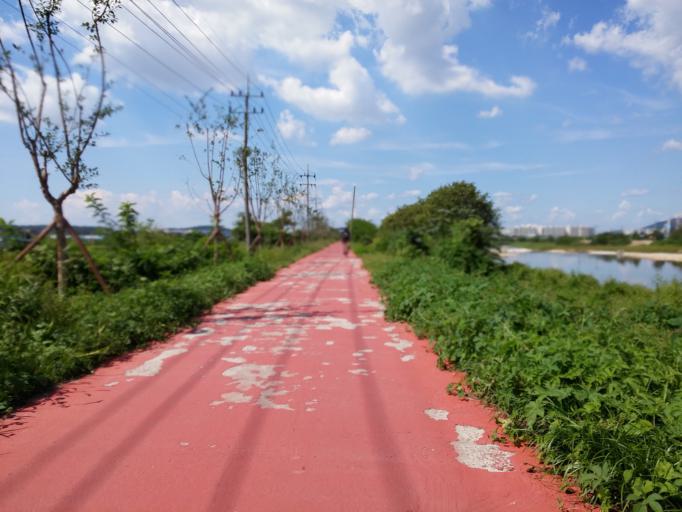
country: KR
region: Chungcheongbuk-do
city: Cheongju-si
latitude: 36.5878
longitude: 127.4994
